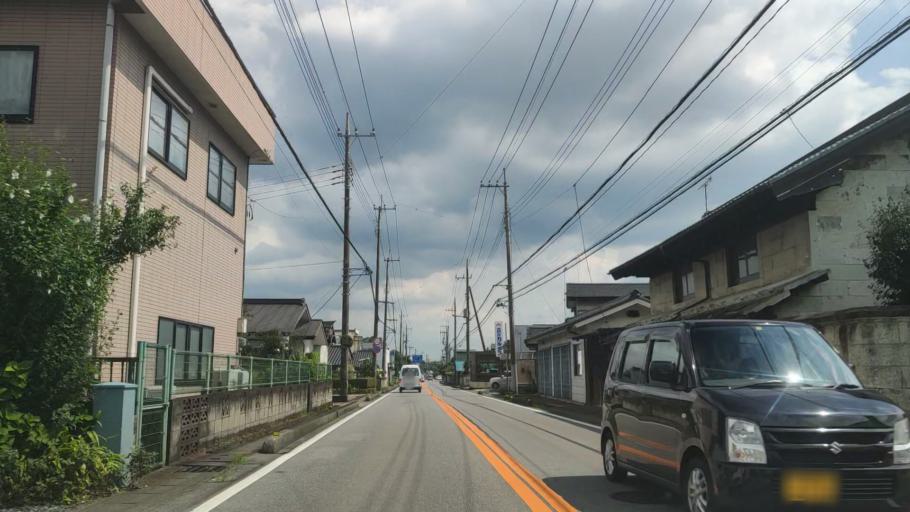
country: JP
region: Tochigi
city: Utsunomiya-shi
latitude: 36.6523
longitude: 139.8425
